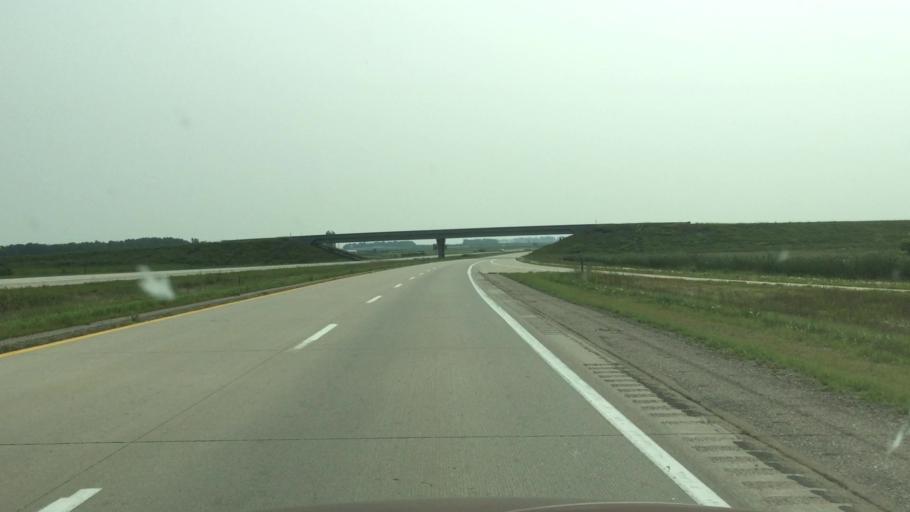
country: US
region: Iowa
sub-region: Osceola County
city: Sibley
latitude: 43.3837
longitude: -95.7449
